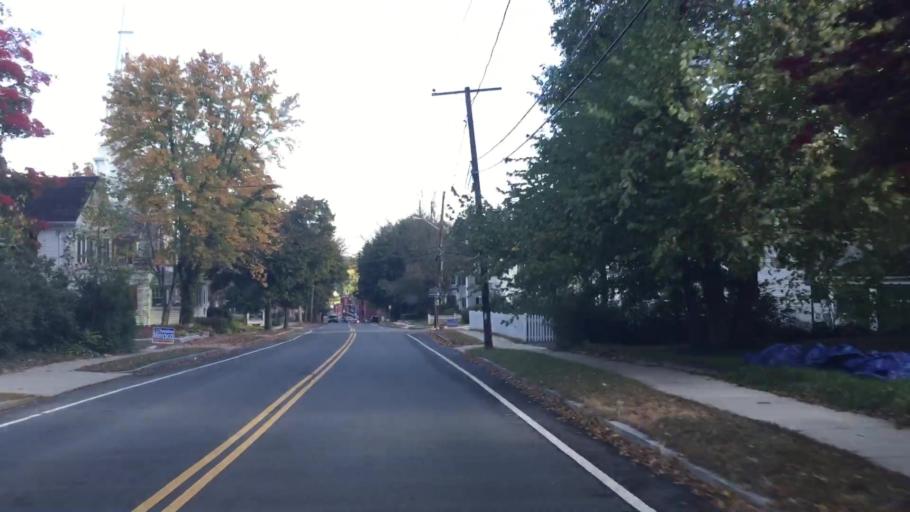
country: US
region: Massachusetts
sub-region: Essex County
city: North Andover
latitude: 42.6978
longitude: -71.1267
